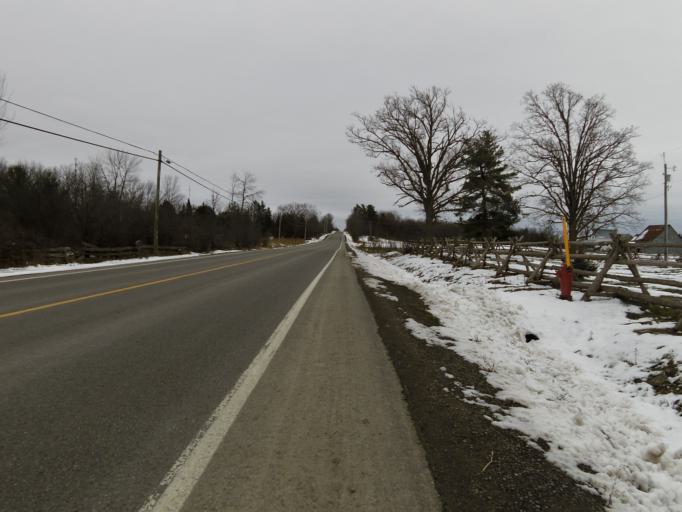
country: CA
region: Ontario
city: Carleton Place
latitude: 45.2410
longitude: -76.2081
